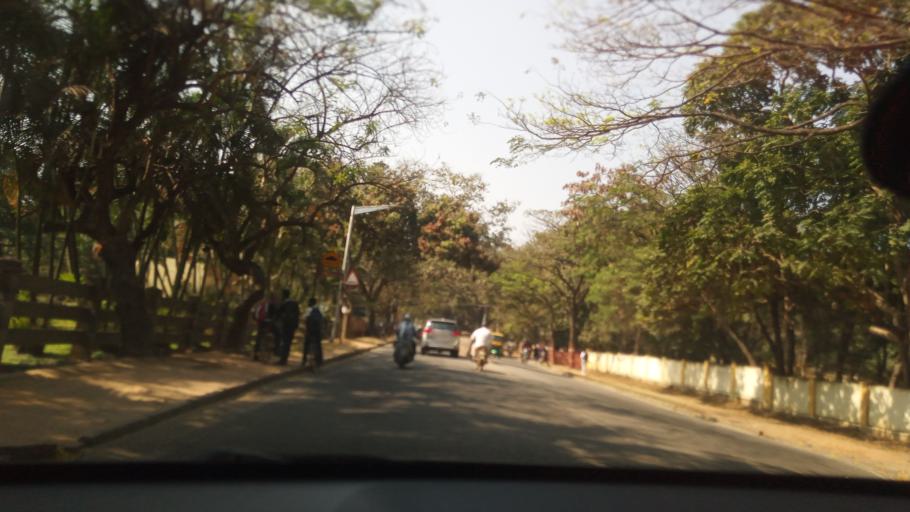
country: IN
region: Karnataka
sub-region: Bangalore Urban
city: Yelahanka
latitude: 13.0488
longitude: 77.5544
